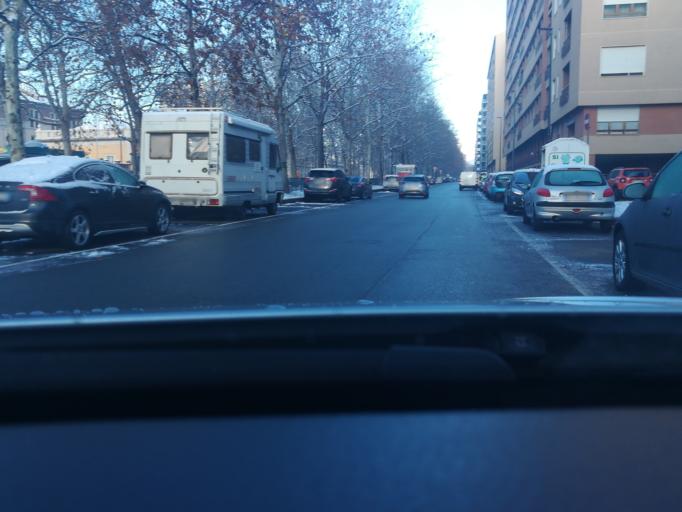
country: IT
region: Piedmont
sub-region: Provincia di Torino
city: Lesna
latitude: 45.0644
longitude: 7.6266
